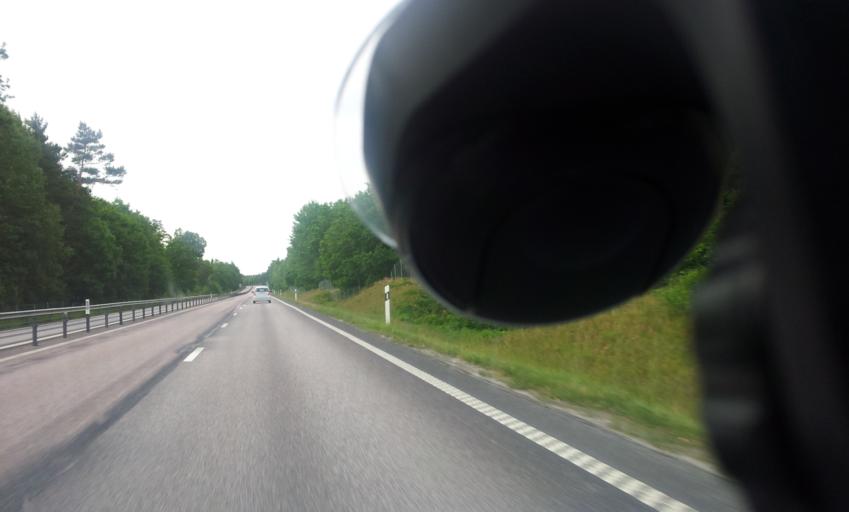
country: SE
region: Kalmar
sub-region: Oskarshamns Kommun
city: Paskallavik
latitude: 57.1736
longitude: 16.4442
